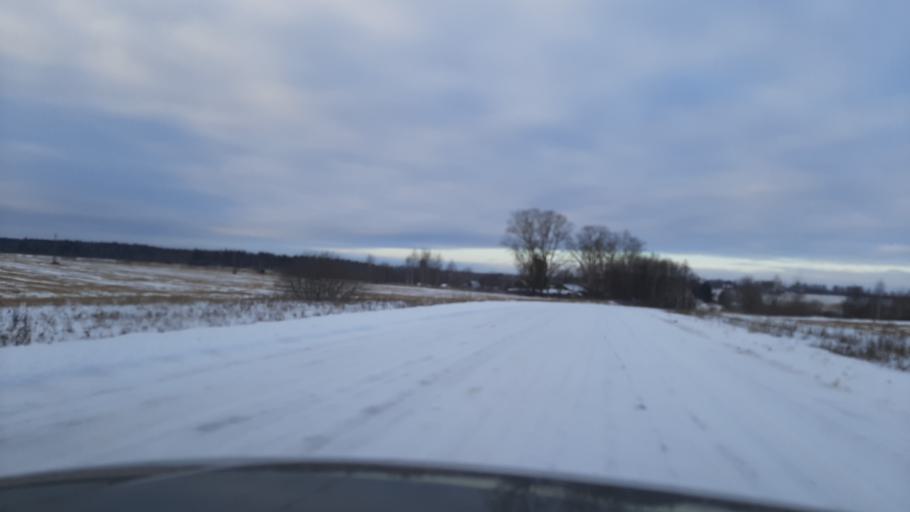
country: RU
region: Kostroma
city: Kosmynino
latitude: 57.4821
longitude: 40.7970
